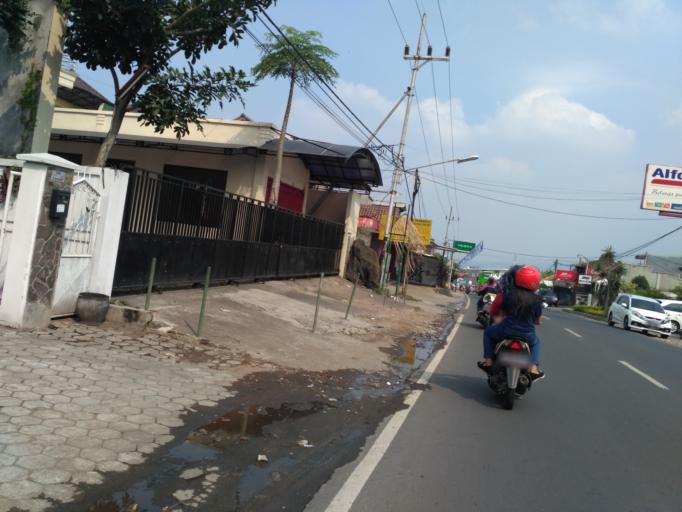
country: ID
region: East Java
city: Batu
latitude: -7.8457
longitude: 112.5283
